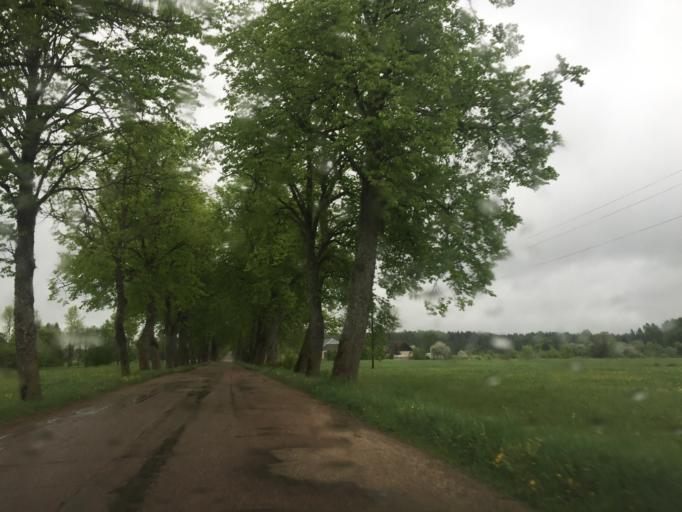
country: LV
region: Ogre
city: Jumprava
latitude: 56.6457
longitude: 24.9217
